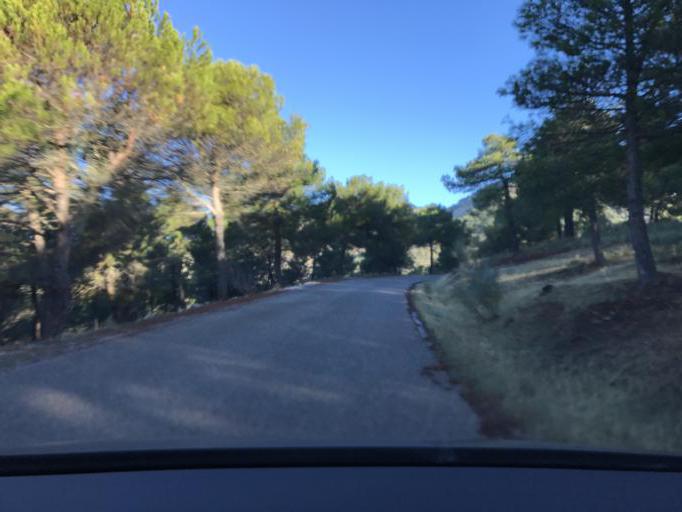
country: ES
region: Andalusia
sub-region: Provincia de Granada
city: Viznar
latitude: 37.2316
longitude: -3.5385
